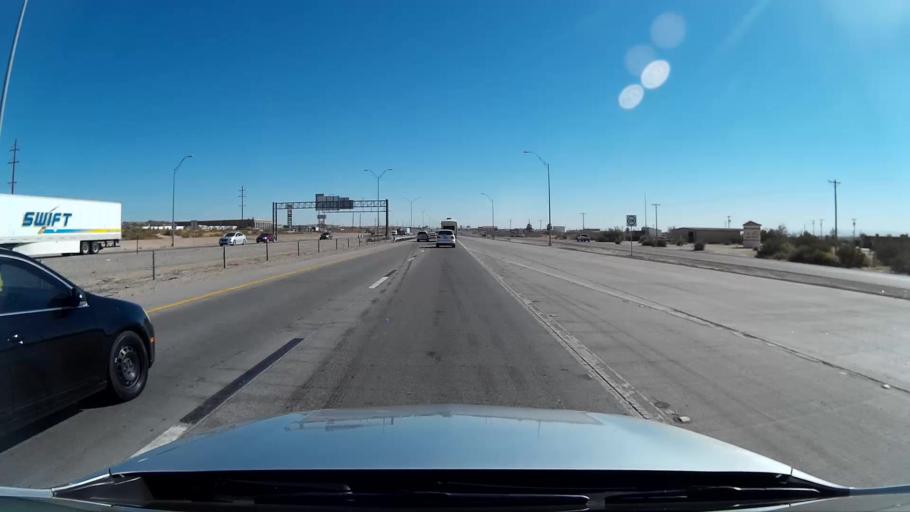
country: US
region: Texas
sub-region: El Paso County
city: Sparks
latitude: 31.6819
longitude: -106.2625
